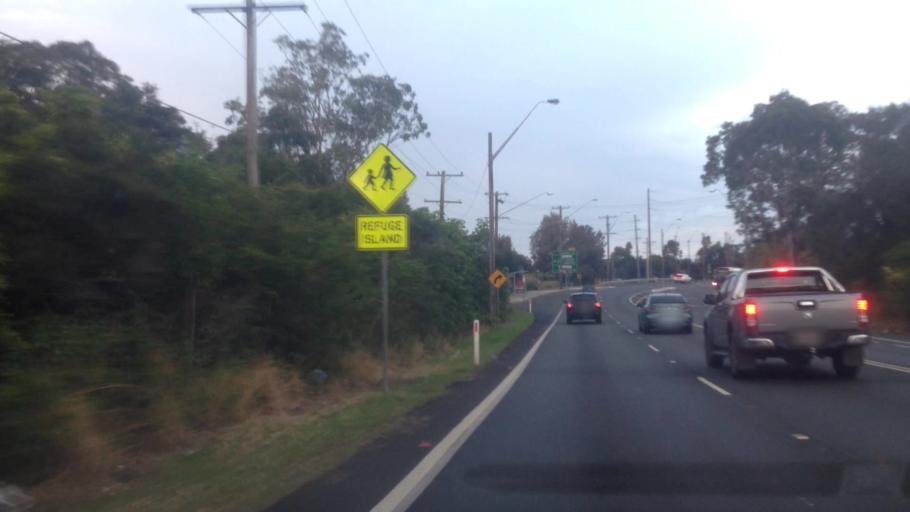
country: AU
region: New South Wales
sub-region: Wyong Shire
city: Kanwal
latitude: -33.2539
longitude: 151.4878
